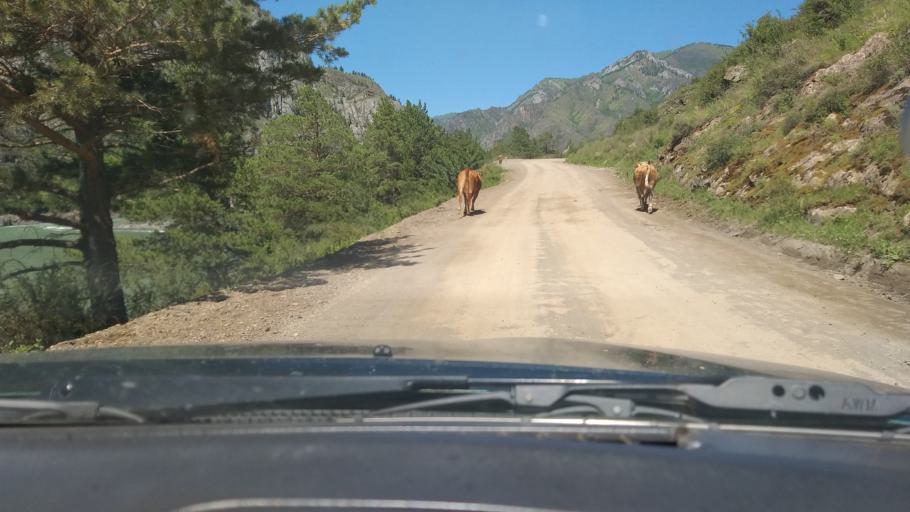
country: RU
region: Altay
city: Chemal
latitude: 51.2059
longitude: 86.0854
